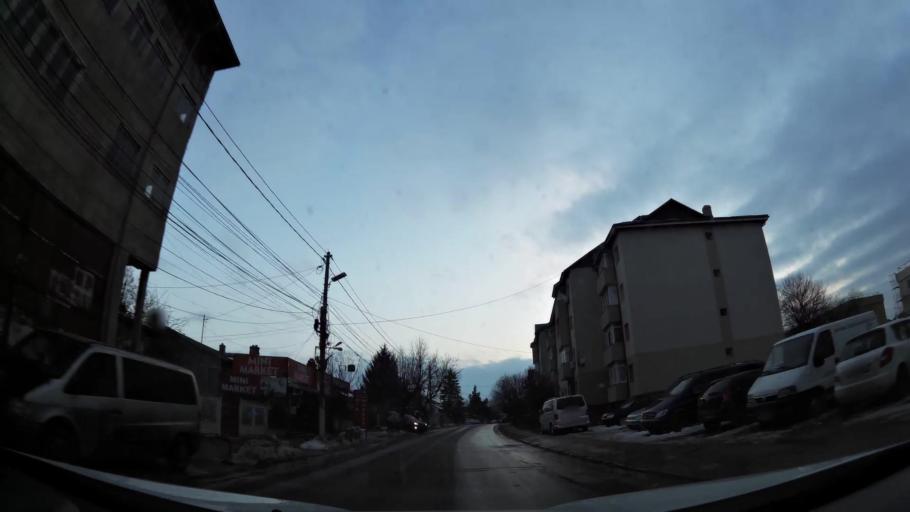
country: RO
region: Ilfov
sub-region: Comuna Popesti-Leordeni
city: Popesti-Leordeni
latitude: 44.3820
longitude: 26.1713
